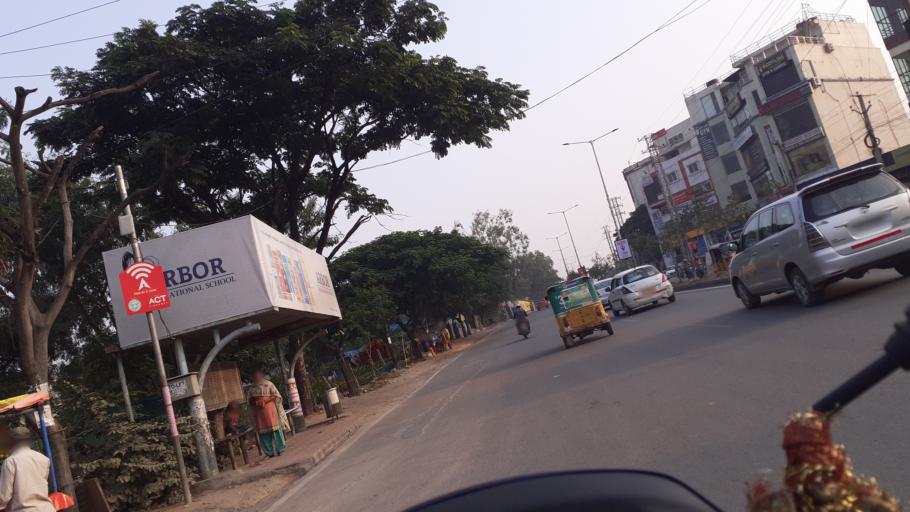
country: IN
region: Telangana
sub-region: Medak
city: Serilingampalle
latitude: 17.4921
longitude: 78.3530
